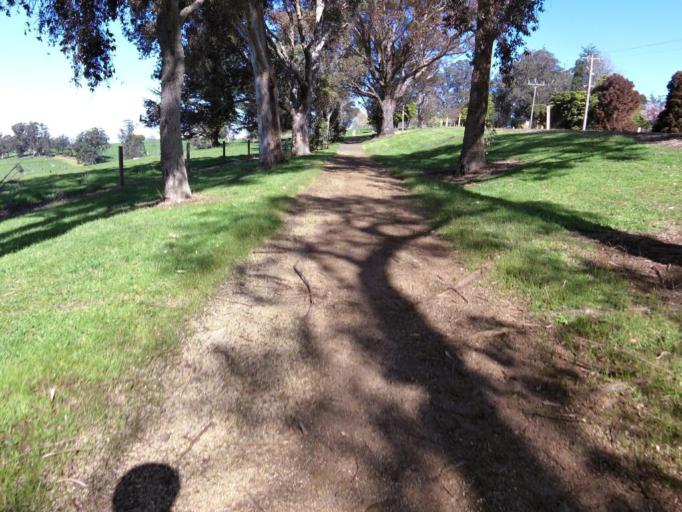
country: AU
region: Victoria
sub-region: Baw Baw
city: Warragul
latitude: -38.0277
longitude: 145.9555
